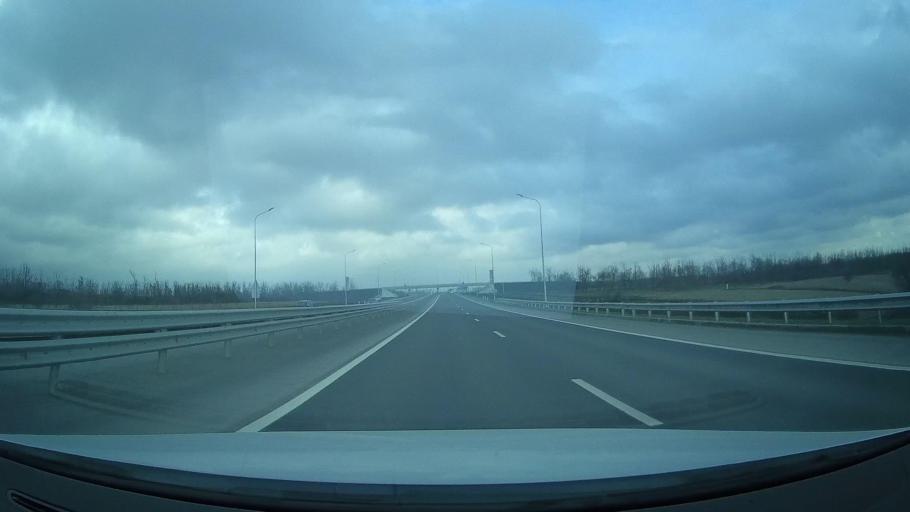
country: RU
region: Rostov
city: Grushevskaya
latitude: 47.4913
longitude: 39.9460
